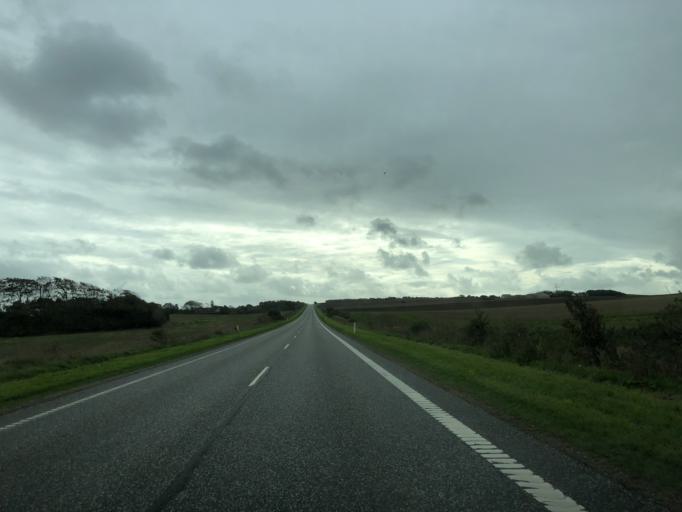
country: DK
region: North Denmark
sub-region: Thisted Kommune
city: Hurup
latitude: 56.7665
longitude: 8.4572
